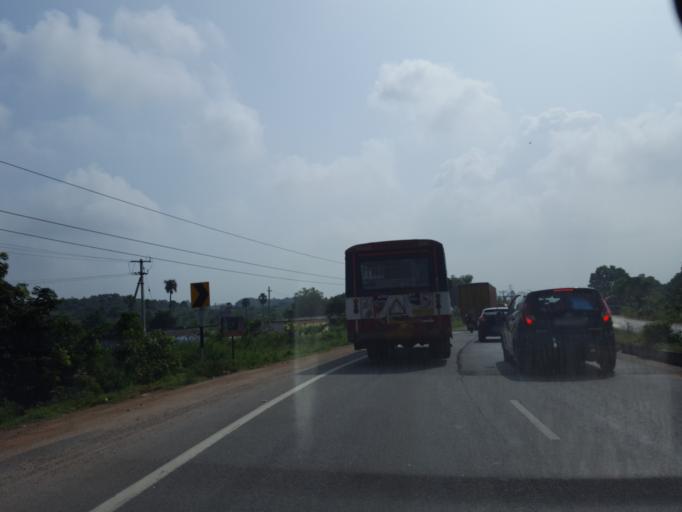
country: IN
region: Telangana
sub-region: Rangareddi
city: Ghatkesar
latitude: 17.3064
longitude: 78.7261
